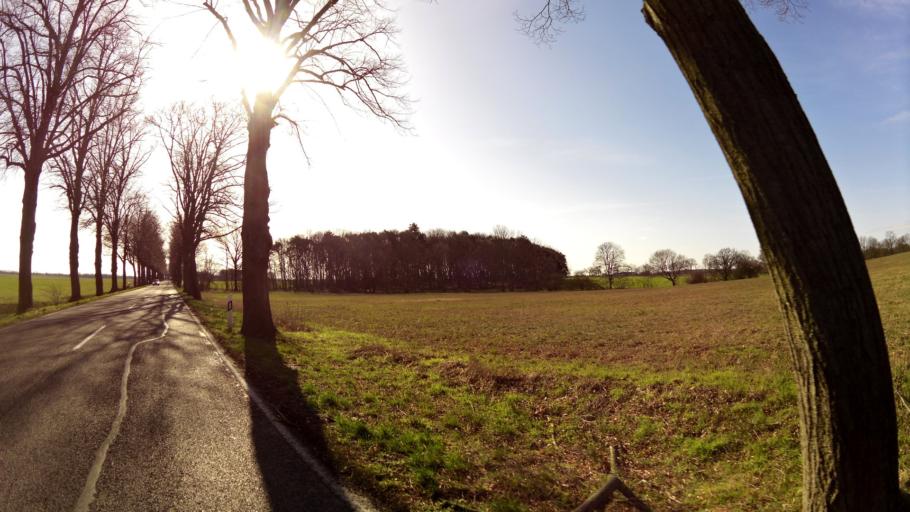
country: DE
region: Brandenburg
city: Mittenwalde
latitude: 52.3035
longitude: 13.5180
